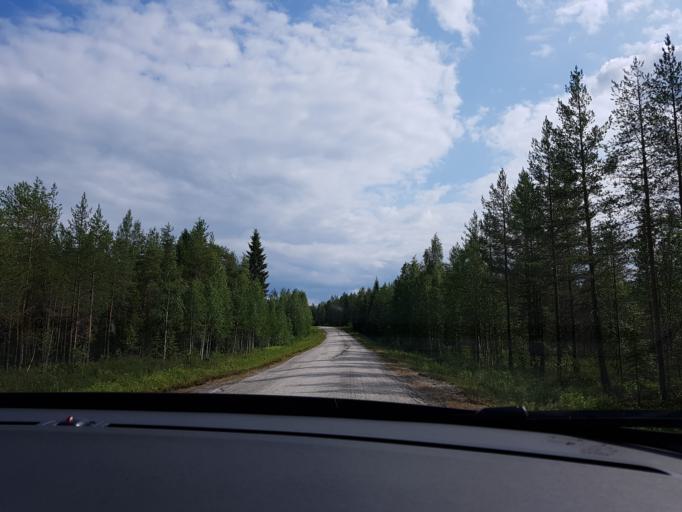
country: FI
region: Kainuu
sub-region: Kehys-Kainuu
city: Kuhmo
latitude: 64.4381
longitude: 29.7074
